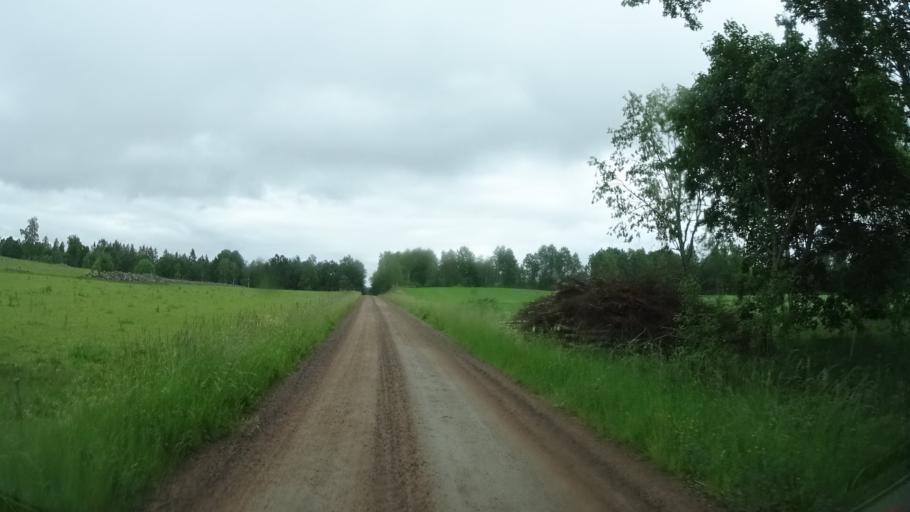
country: SE
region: Joenkoeping
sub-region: Eksjo Kommun
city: Mariannelund
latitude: 57.6185
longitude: 15.6468
